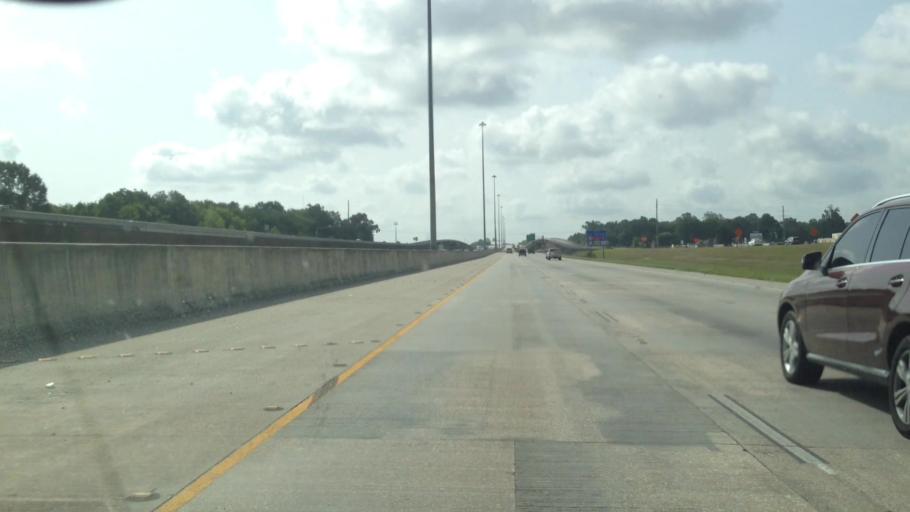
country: US
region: Louisiana
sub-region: East Baton Rouge Parish
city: Inniswold
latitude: 30.3902
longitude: -91.0784
